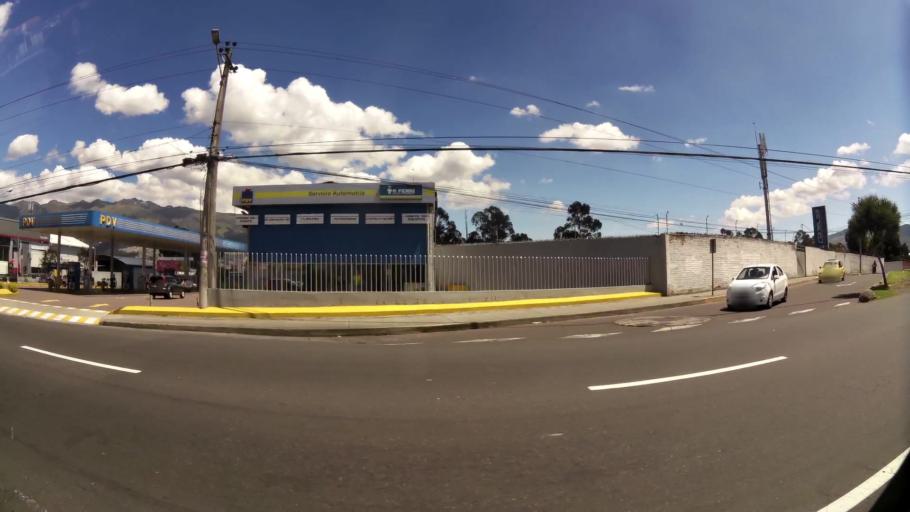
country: EC
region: Pichincha
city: Quito
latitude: -0.1107
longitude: -78.4789
